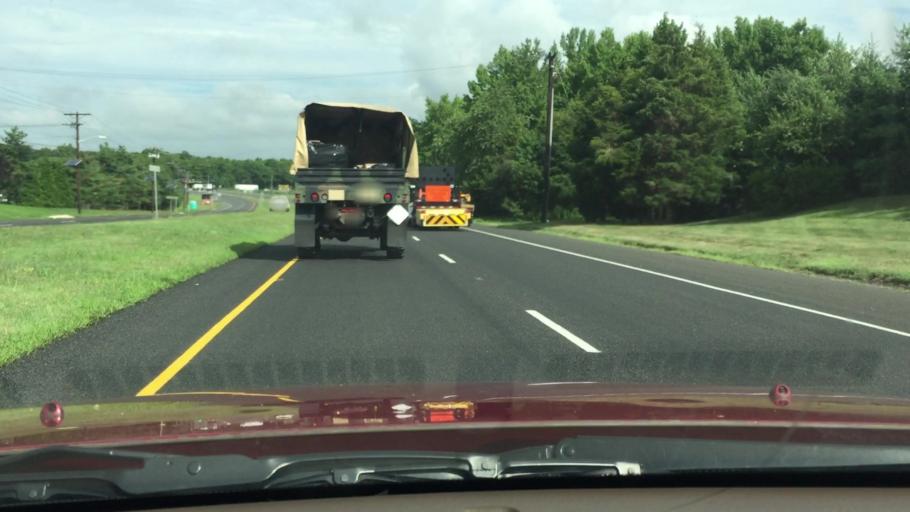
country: US
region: New Jersey
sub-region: Burlington County
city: Bordentown
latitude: 40.1106
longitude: -74.7010
